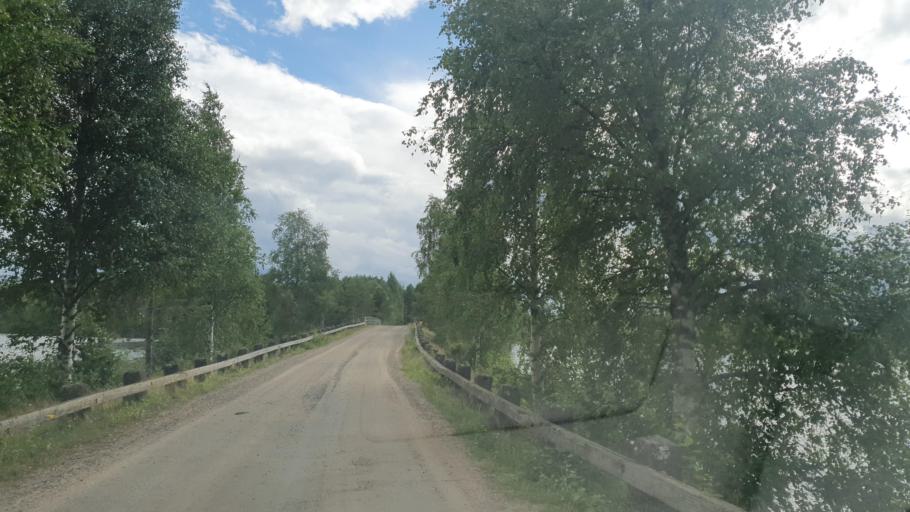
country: FI
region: Kainuu
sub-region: Kehys-Kainuu
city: Kuhmo
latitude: 64.0876
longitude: 29.0959
